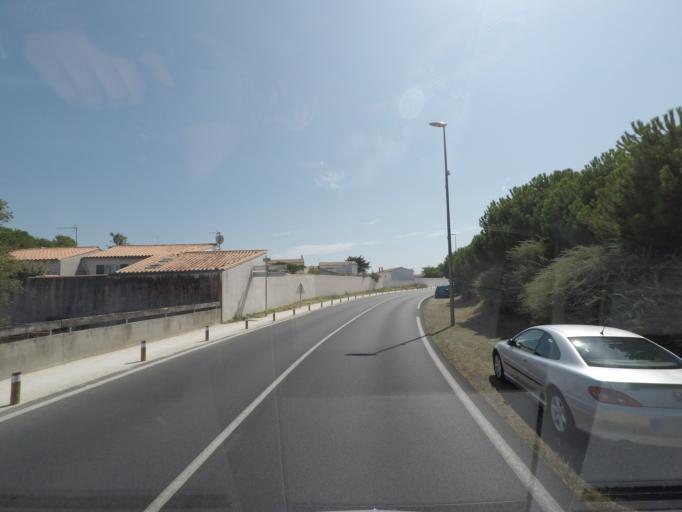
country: FR
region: Poitou-Charentes
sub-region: Departement de la Charente-Maritime
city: Rivedoux-Plage
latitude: 46.1586
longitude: -1.2653
